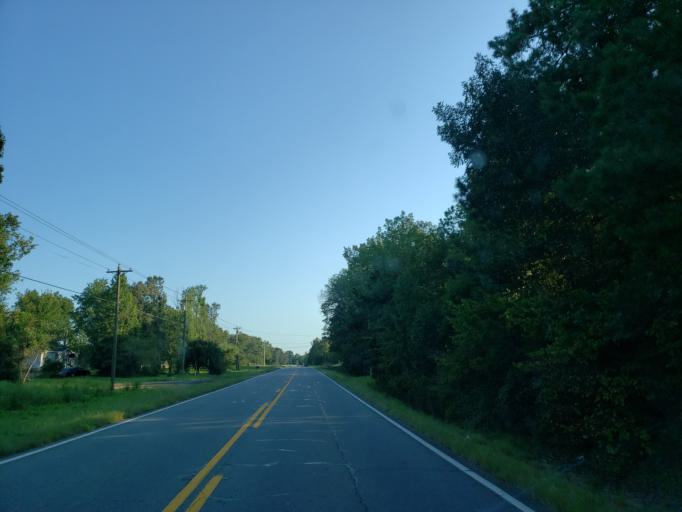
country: US
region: Georgia
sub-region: Murray County
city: Chatsworth
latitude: 34.7138
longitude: -84.8188
